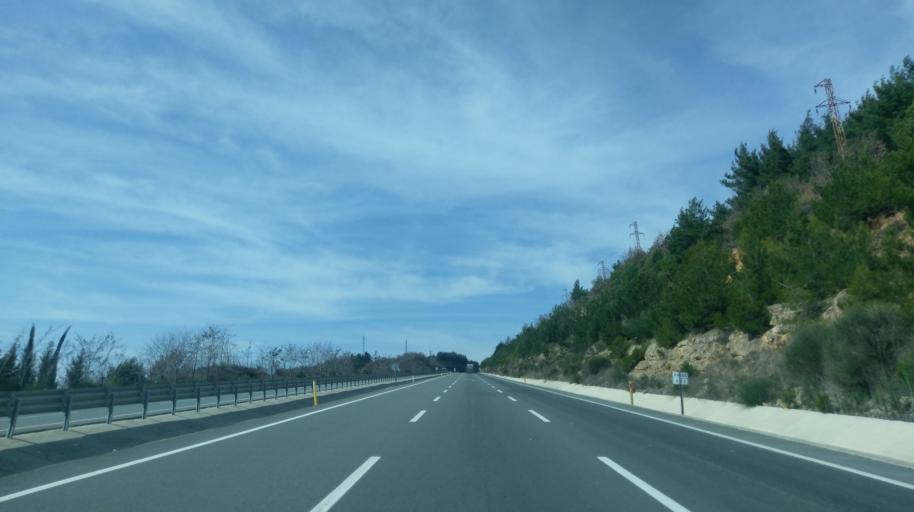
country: TR
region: Canakkale
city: Evrese
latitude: 40.7080
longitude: 26.7774
